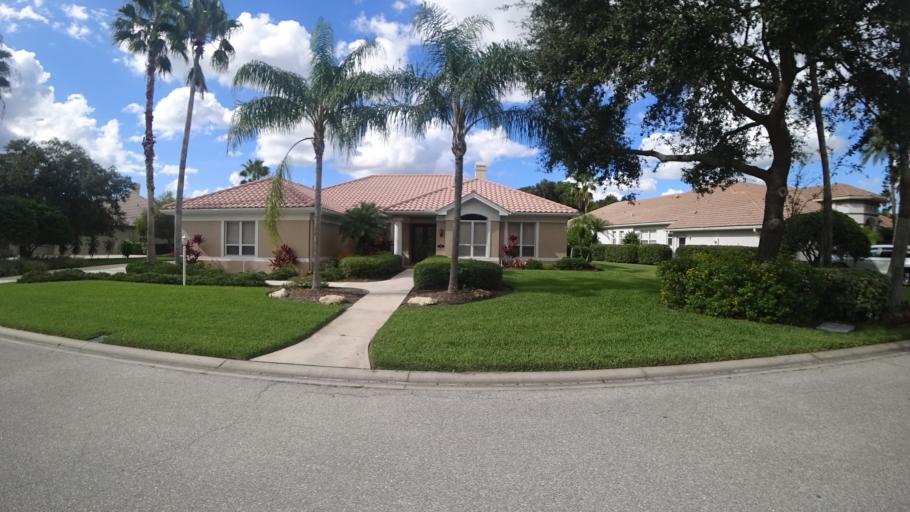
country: US
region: Florida
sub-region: Sarasota County
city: The Meadows
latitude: 27.3966
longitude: -82.4188
